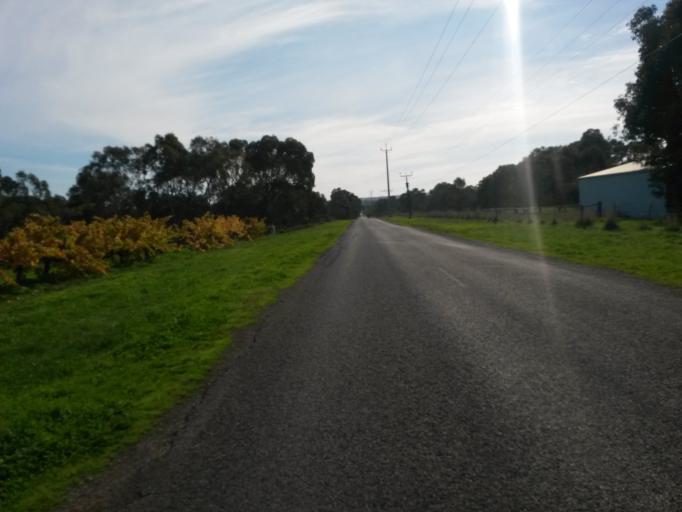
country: AU
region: South Australia
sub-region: Onkaparinga
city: McLaren Vale
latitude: -35.2333
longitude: 138.5705
